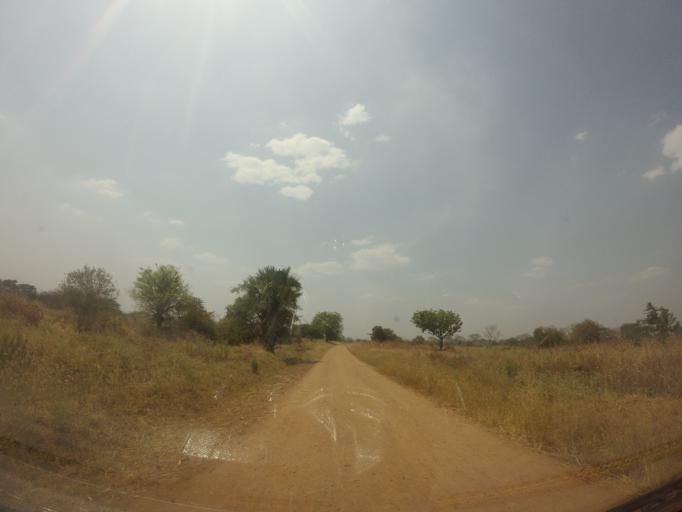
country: UG
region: Northern Region
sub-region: Arua District
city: Arua
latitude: 2.8848
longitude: 31.2058
